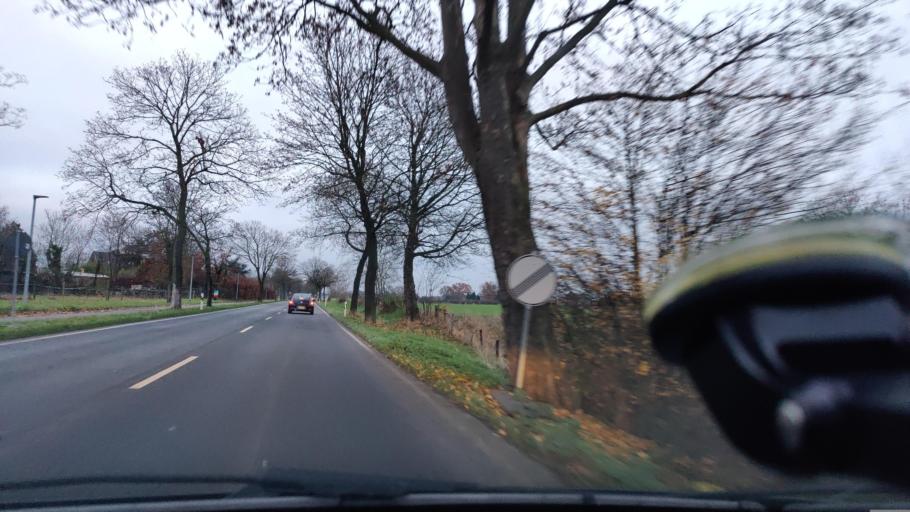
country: DE
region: North Rhine-Westphalia
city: Rheinberg
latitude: 51.5389
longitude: 6.6187
